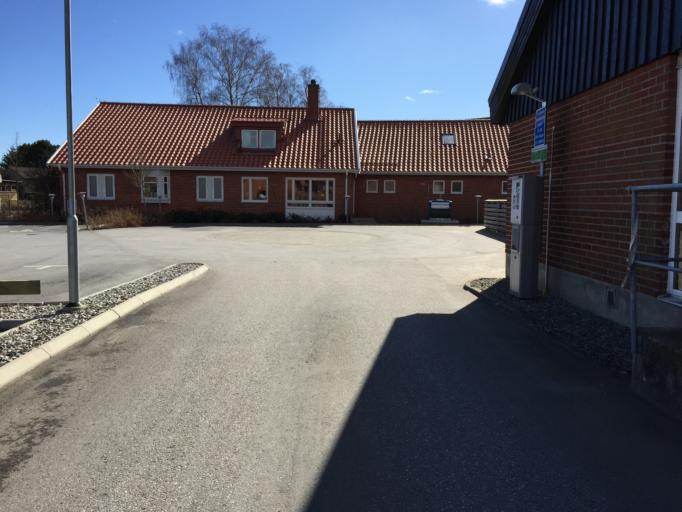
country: SE
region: Skane
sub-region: Lunds Kommun
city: Veberod
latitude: 55.6339
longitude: 13.4939
